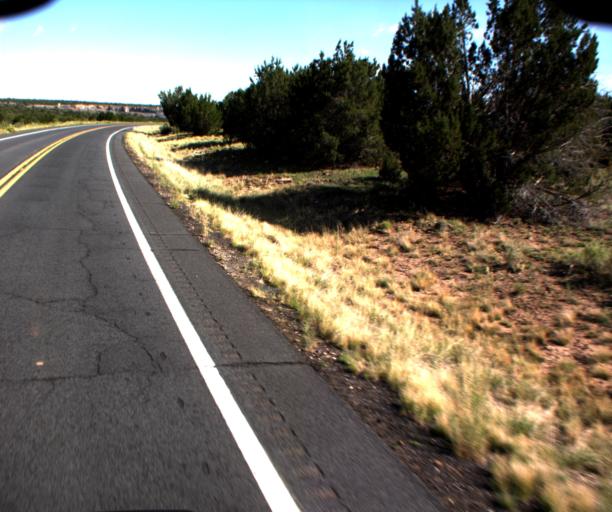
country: US
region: Arizona
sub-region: Coconino County
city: Williams
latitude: 35.4744
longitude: -112.1769
